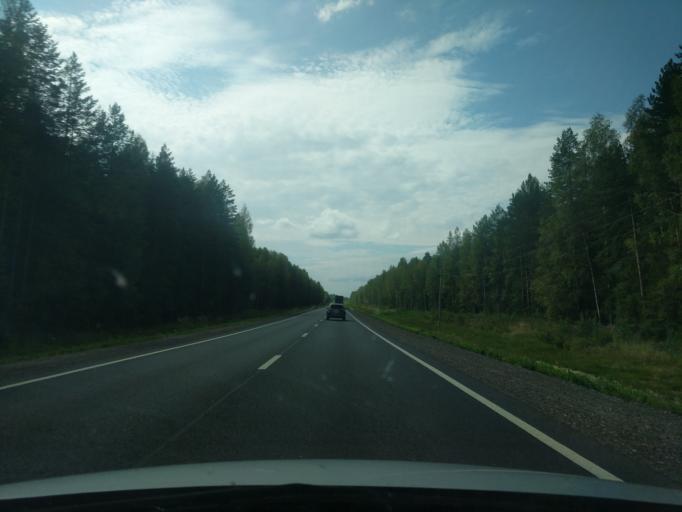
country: RU
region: Kostroma
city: Kadyy
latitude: 57.8077
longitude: 43.2191
